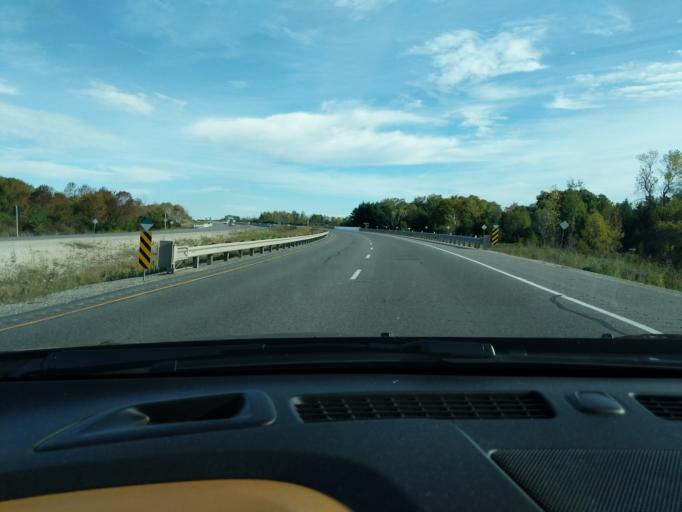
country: CA
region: Ontario
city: Collingwood
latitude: 44.4831
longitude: -80.1714
